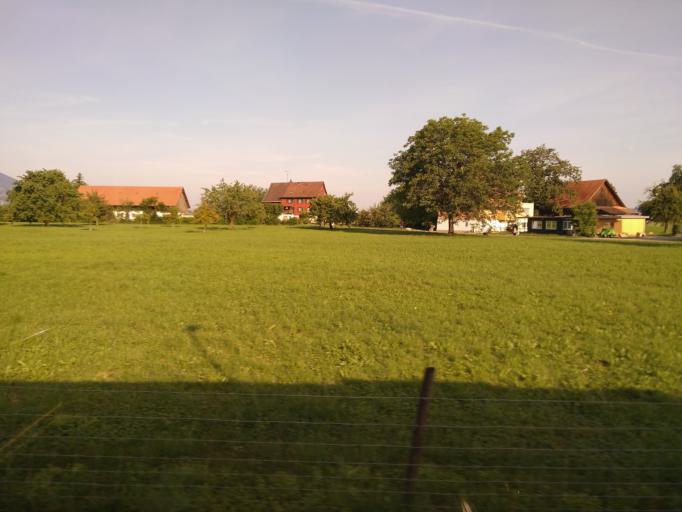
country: CH
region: Schwyz
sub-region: Bezirk March
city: Lachen
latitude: 47.2010
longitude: 8.8857
